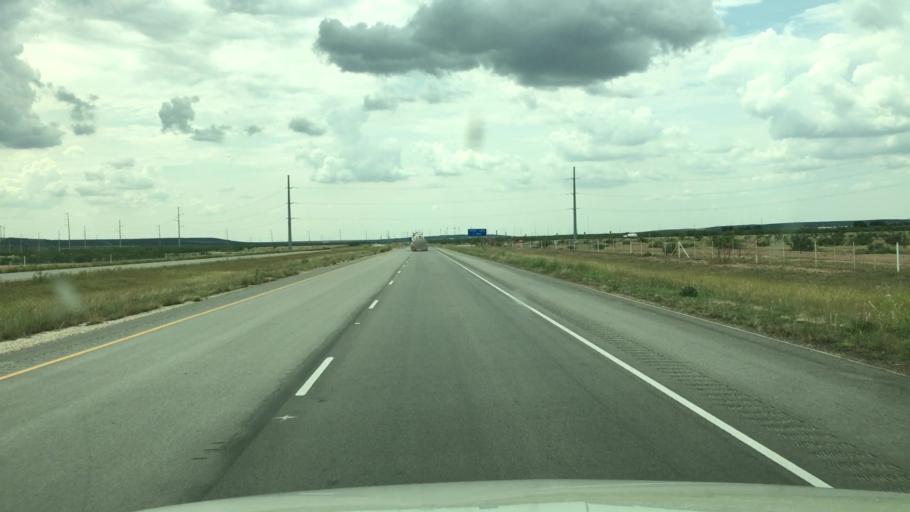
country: US
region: Texas
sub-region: Sterling County
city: Sterling City
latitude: 31.9598
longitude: -101.2096
